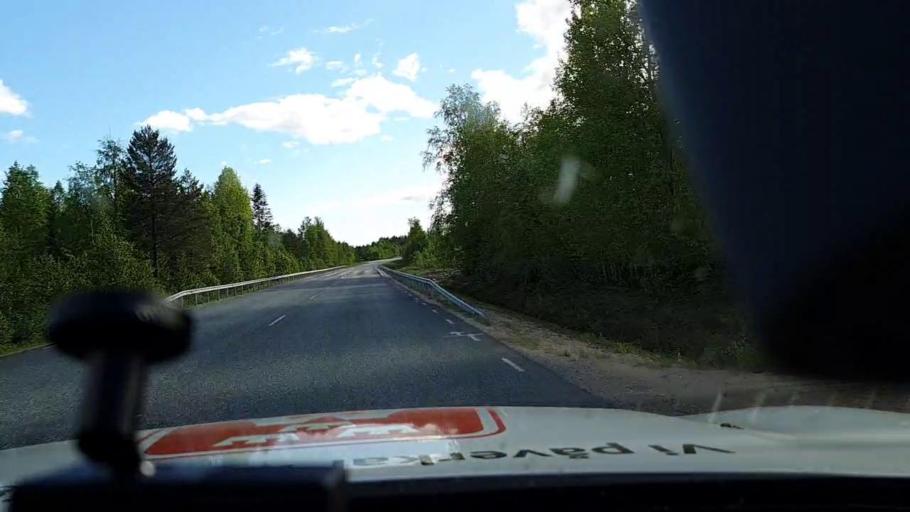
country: FI
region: Lapland
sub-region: Torniolaakso
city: Ylitornio
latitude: 66.3389
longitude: 23.6451
